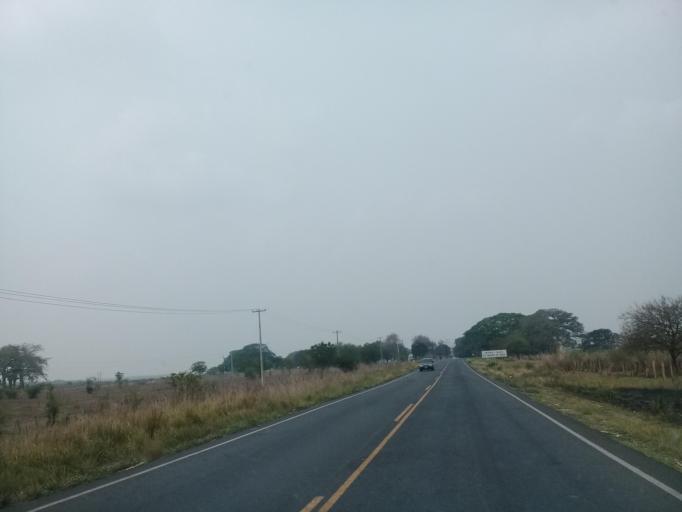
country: MX
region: Veracruz
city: Jamapa
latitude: 18.9140
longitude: -96.1996
